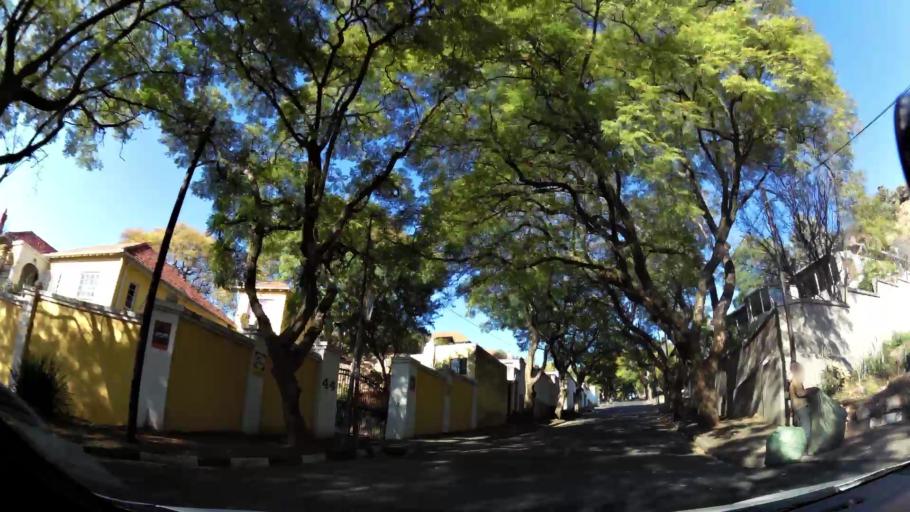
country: ZA
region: Gauteng
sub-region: City of Johannesburg Metropolitan Municipality
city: Johannesburg
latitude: -26.1937
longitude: 28.0880
